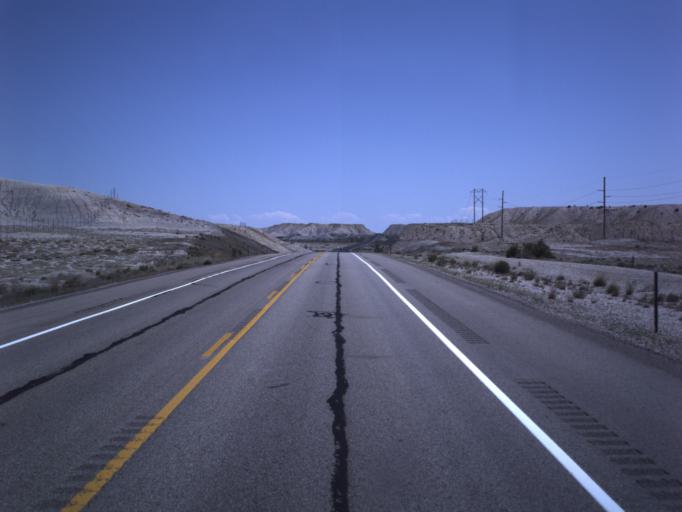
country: US
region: Utah
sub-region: Emery County
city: Ferron
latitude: 38.9499
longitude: -111.2105
